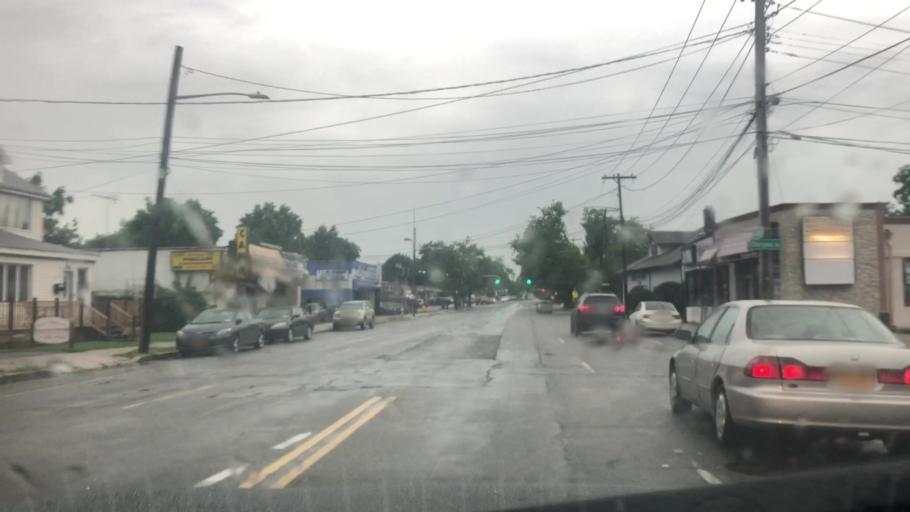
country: US
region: New York
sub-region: Nassau County
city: Uniondale
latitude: 40.7007
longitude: -73.5938
